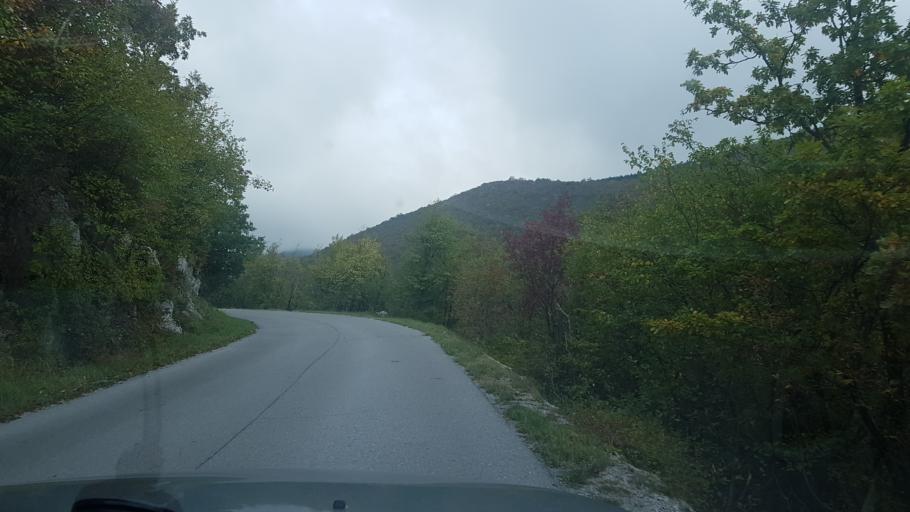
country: SI
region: Hrpelje-Kozina
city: Kozina
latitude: 45.5131
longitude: 13.9620
